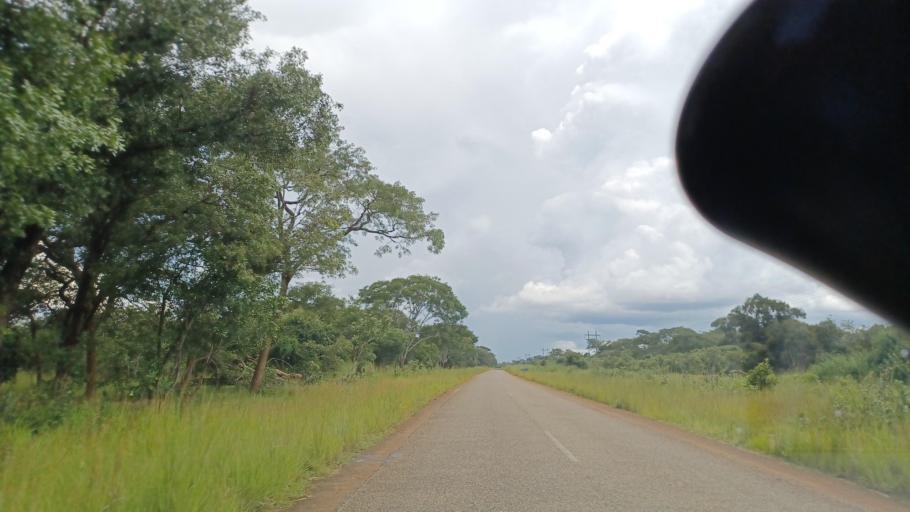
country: ZM
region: North-Western
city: Kasempa
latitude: -13.1435
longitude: 25.8775
